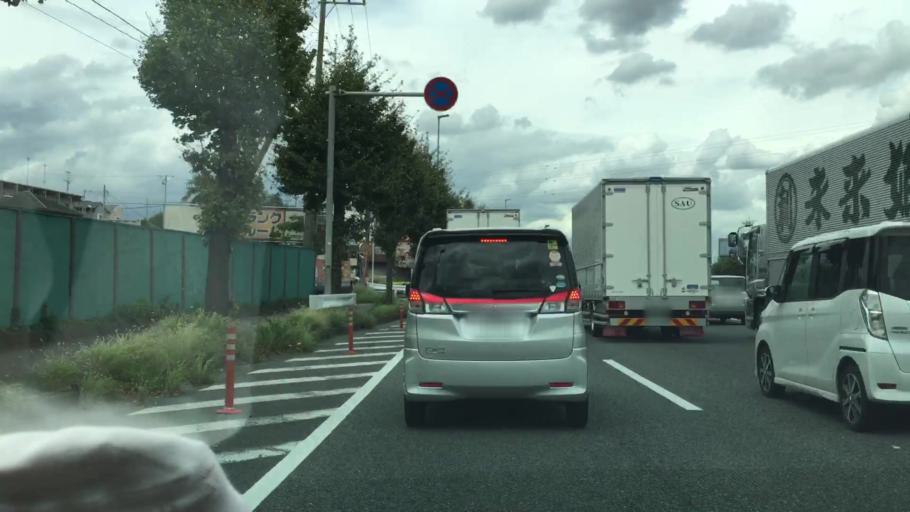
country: JP
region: Saitama
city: Yono
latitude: 35.9109
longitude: 139.5938
